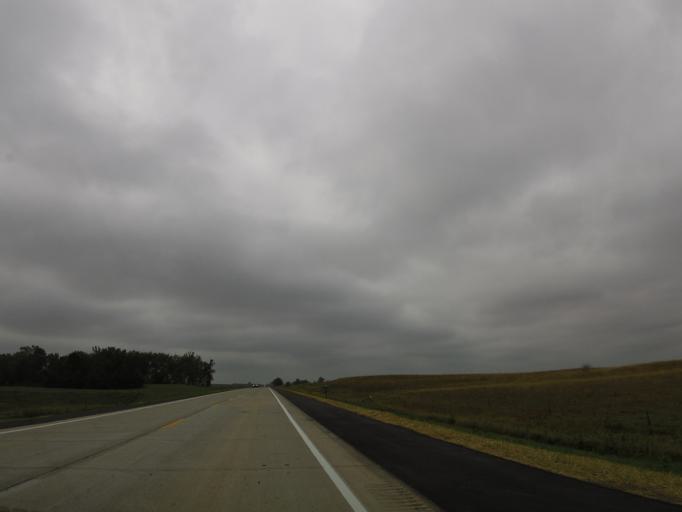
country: US
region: South Dakota
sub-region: Deuel County
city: Clear Lake
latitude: 44.8901
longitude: -96.7004
